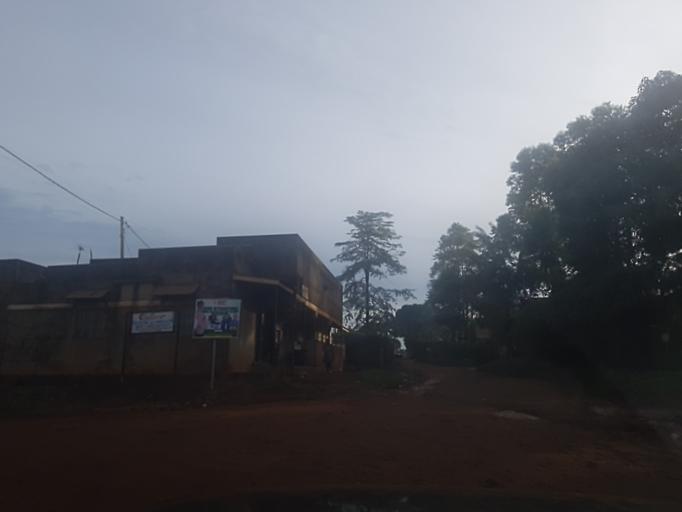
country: UG
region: Central Region
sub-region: Mukono District
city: Mukono
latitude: 0.3772
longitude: 32.7136
